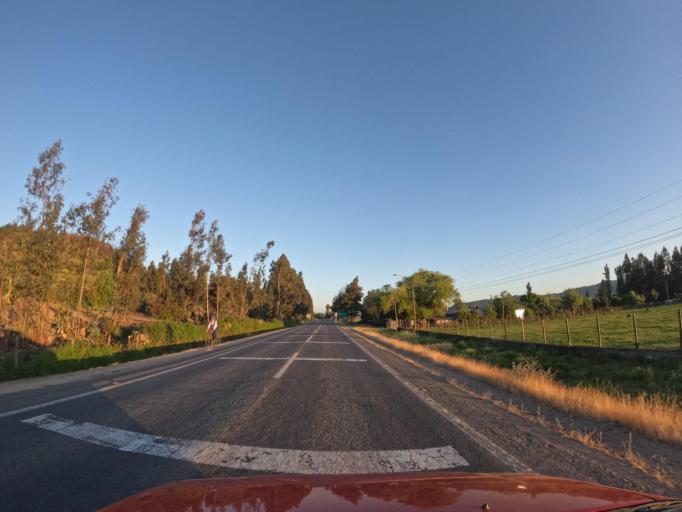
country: CL
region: Maule
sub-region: Provincia de Talca
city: Talca
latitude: -35.0873
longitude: -71.6657
